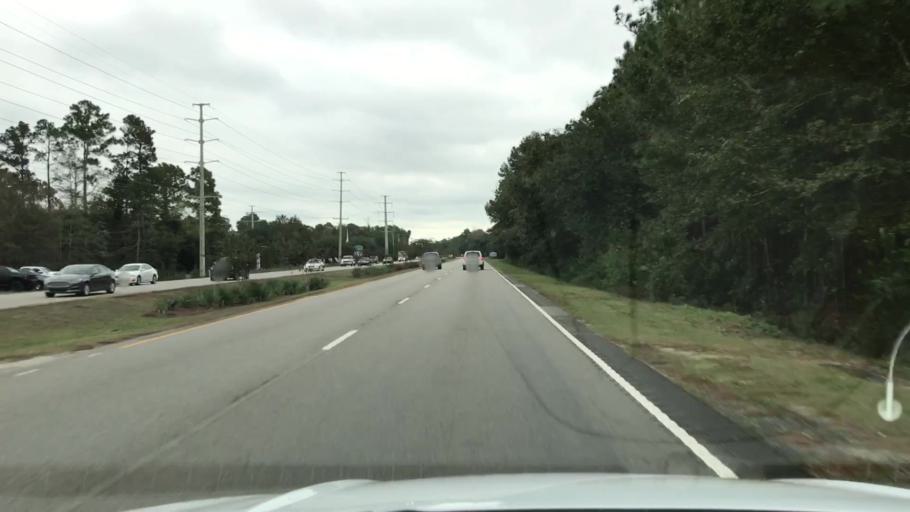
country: US
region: South Carolina
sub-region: Georgetown County
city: Georgetown
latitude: 33.4260
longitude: -79.1562
